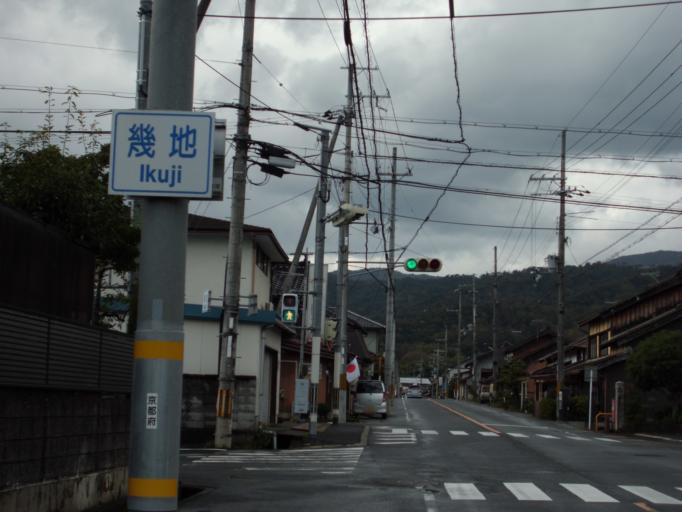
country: JP
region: Kyoto
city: Miyazu
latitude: 35.5304
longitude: 135.0912
